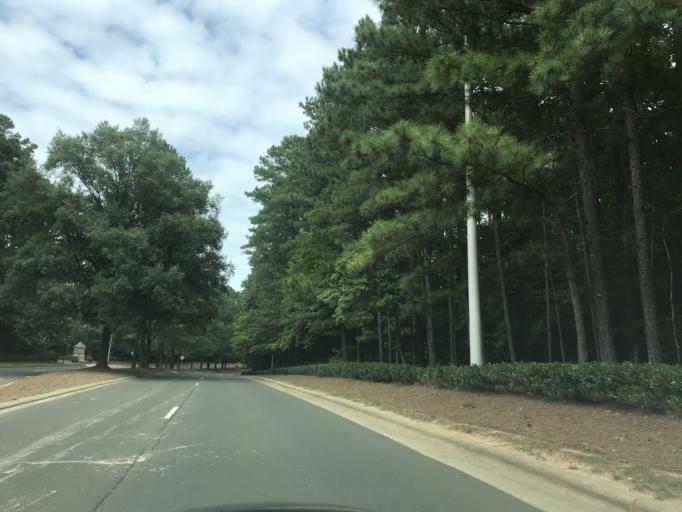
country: US
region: North Carolina
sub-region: Wake County
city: Apex
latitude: 35.7218
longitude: -78.7970
